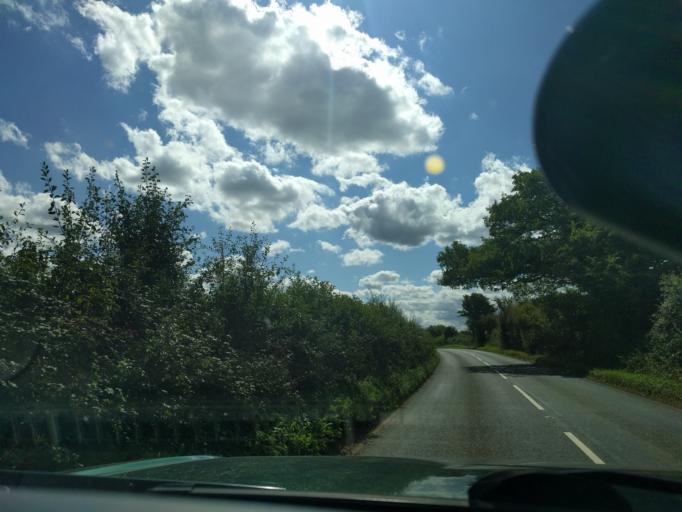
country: GB
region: England
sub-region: Wiltshire
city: Box
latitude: 51.3863
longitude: -2.2344
